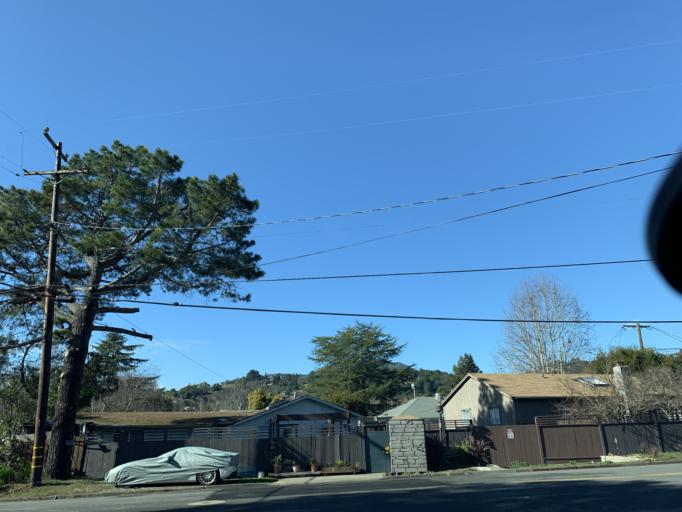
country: US
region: California
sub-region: Marin County
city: Strawberry
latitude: 37.9047
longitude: -122.5183
